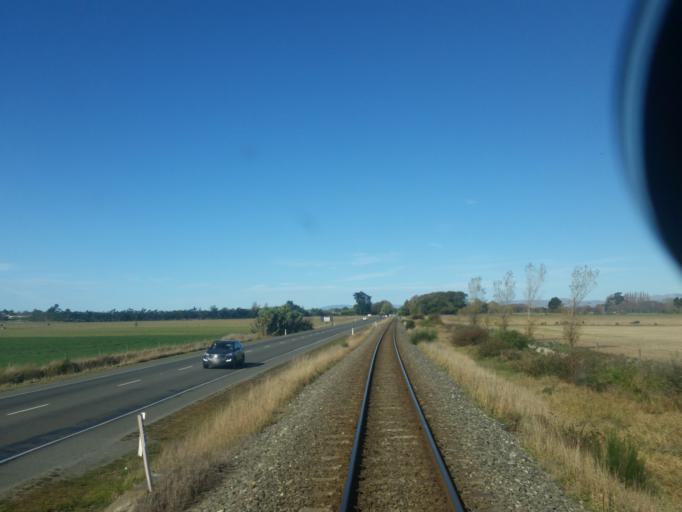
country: NZ
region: Canterbury
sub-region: Waimakariri District
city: Kaiapoi
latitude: -43.3653
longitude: 172.6361
